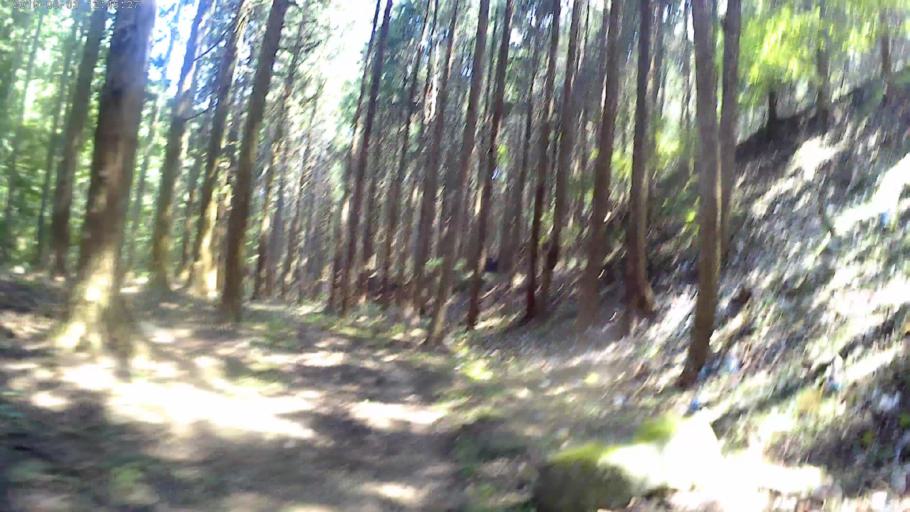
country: JP
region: Yamanashi
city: Enzan
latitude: 35.6056
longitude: 138.7947
